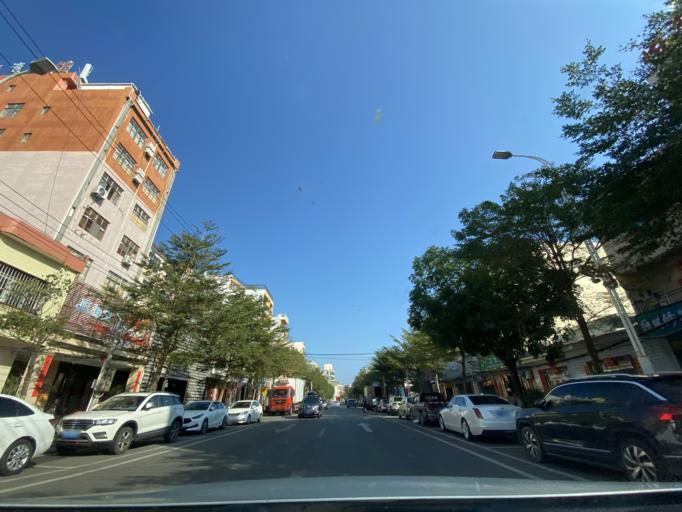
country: CN
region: Hainan
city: Xincun
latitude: 18.4138
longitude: 109.9636
